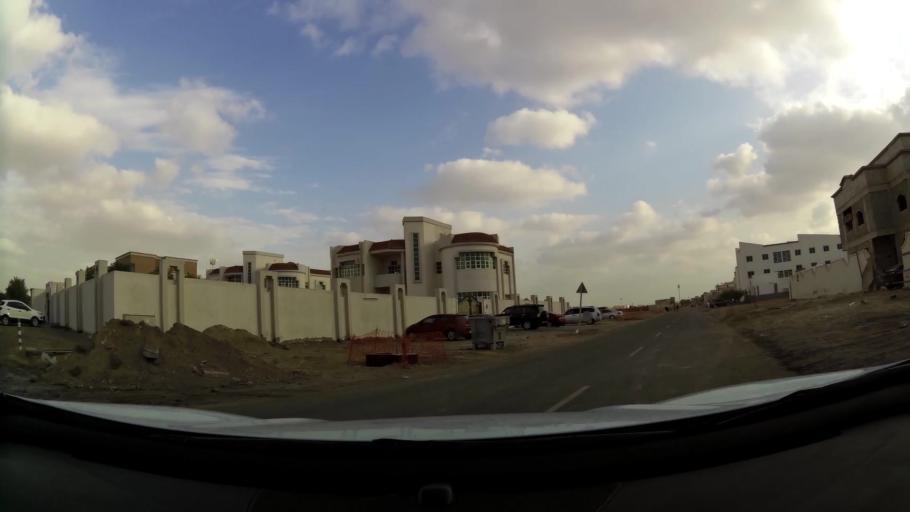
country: AE
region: Abu Dhabi
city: Abu Dhabi
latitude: 24.3707
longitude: 54.5438
